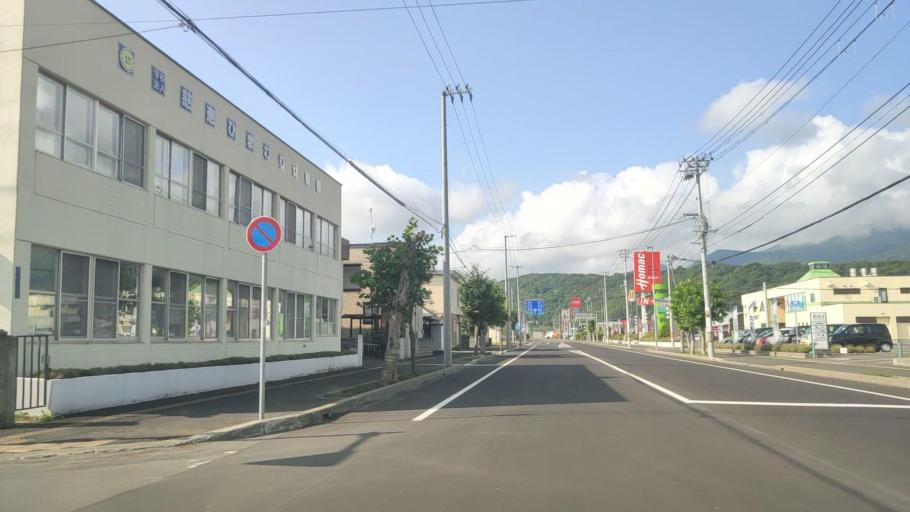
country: JP
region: Hokkaido
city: Shimo-furano
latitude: 43.3459
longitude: 142.3826
